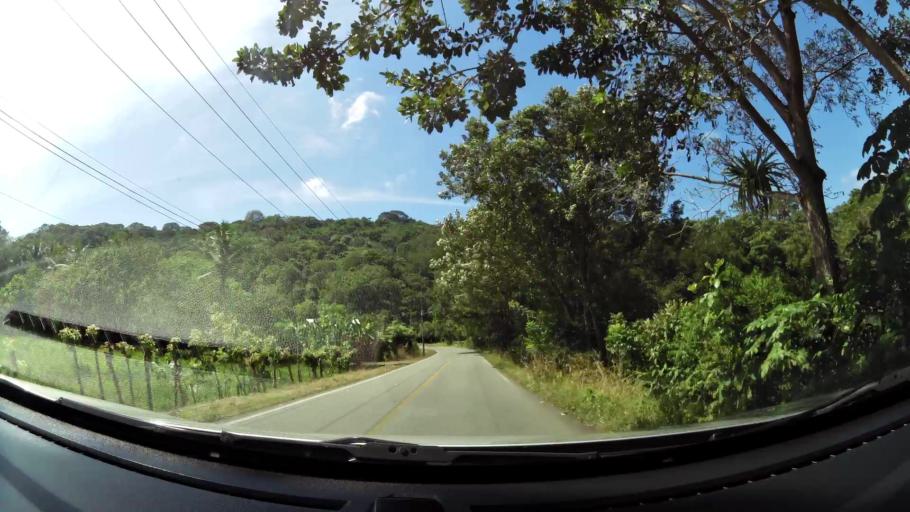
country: CR
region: San Jose
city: San Isidro
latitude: 9.2799
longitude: -83.8595
